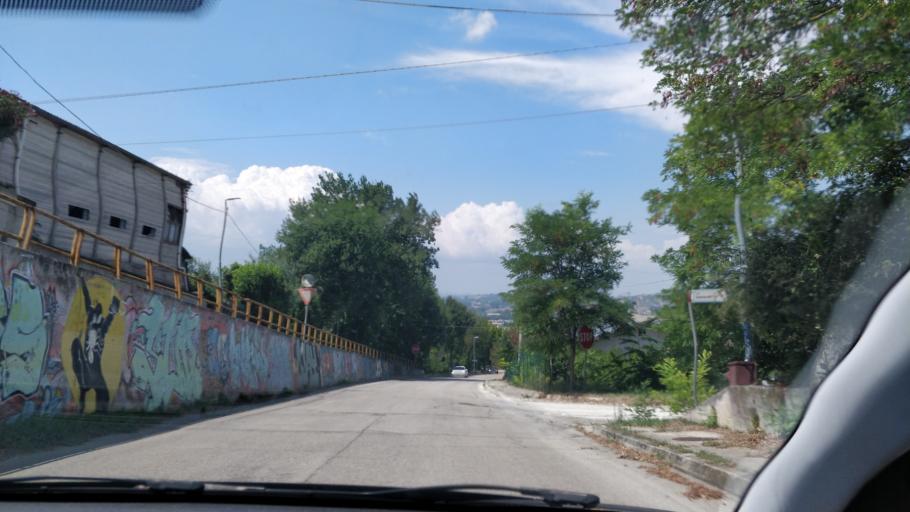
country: IT
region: Abruzzo
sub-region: Provincia di Chieti
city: Sambuceto
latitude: 42.4075
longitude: 14.1845
